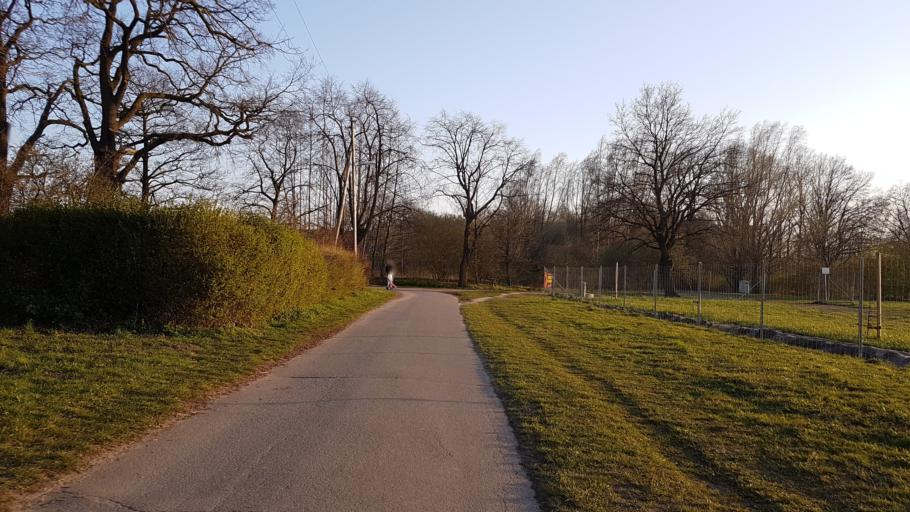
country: DE
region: Lower Saxony
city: Langenhagen
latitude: 52.4267
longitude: 9.6994
